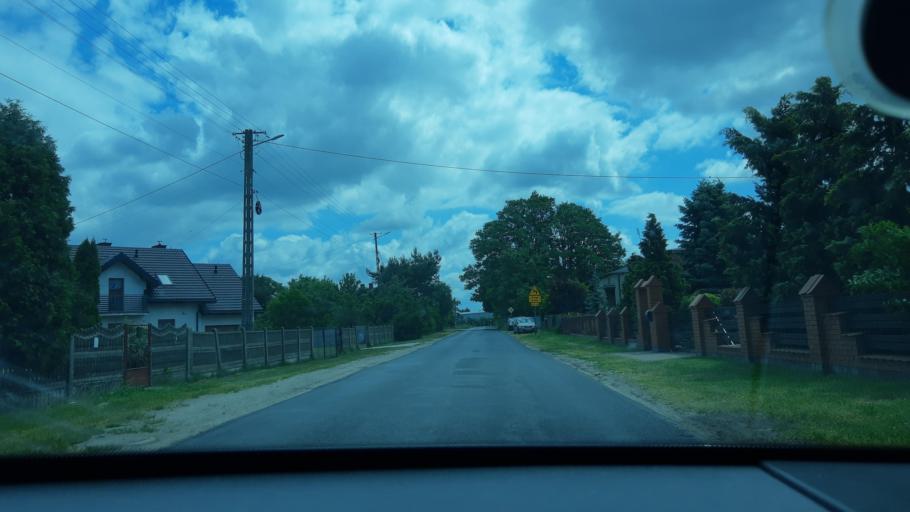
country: PL
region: Lodz Voivodeship
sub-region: Powiat zdunskowolski
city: Zapolice
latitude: 51.5390
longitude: 18.8053
